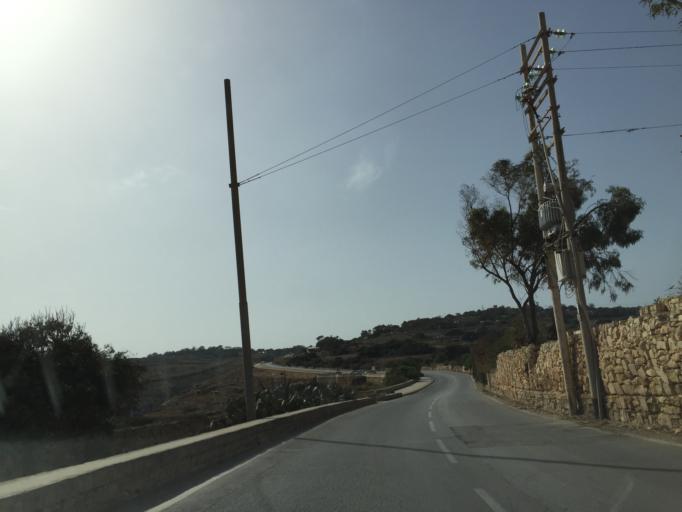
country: MT
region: Il-Qrendi
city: Qrendi
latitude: 35.8226
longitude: 14.4545
